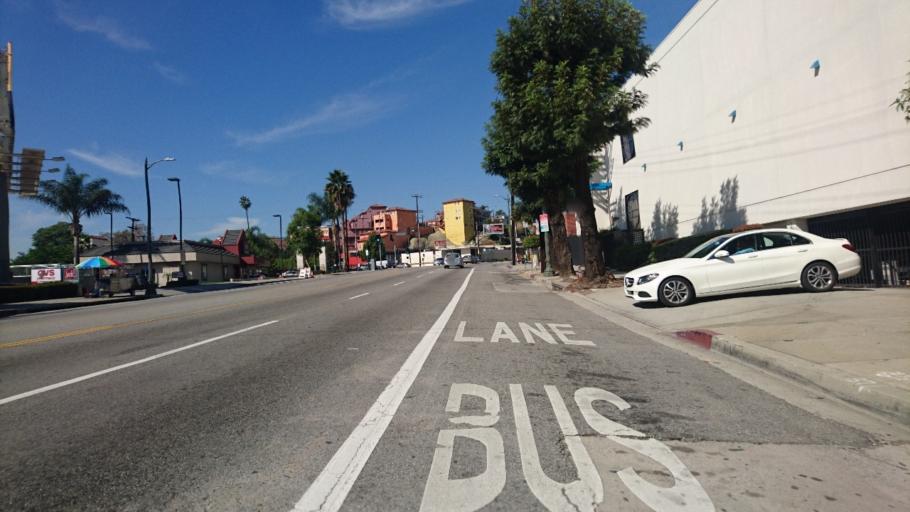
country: US
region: California
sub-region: Los Angeles County
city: Los Angeles
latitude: 34.0645
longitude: -118.2484
